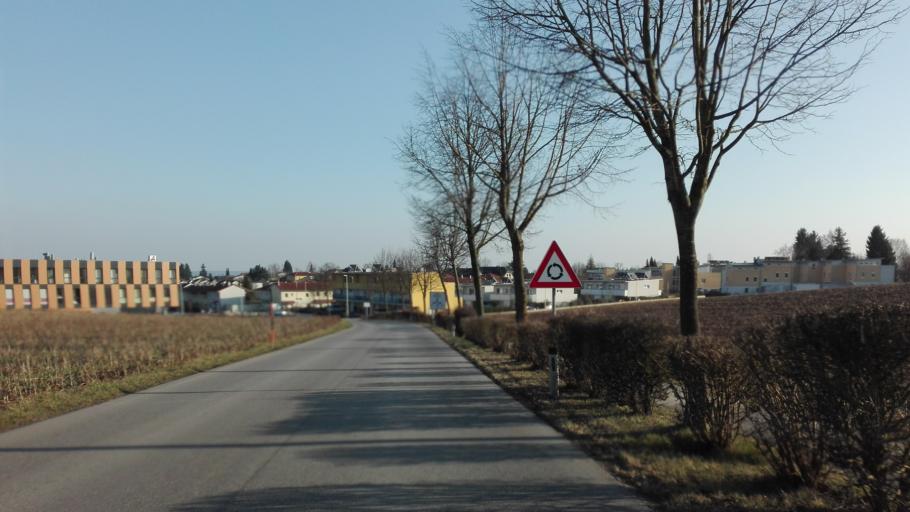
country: AT
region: Upper Austria
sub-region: Politischer Bezirk Linz-Land
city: Leonding
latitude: 48.2875
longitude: 14.2527
